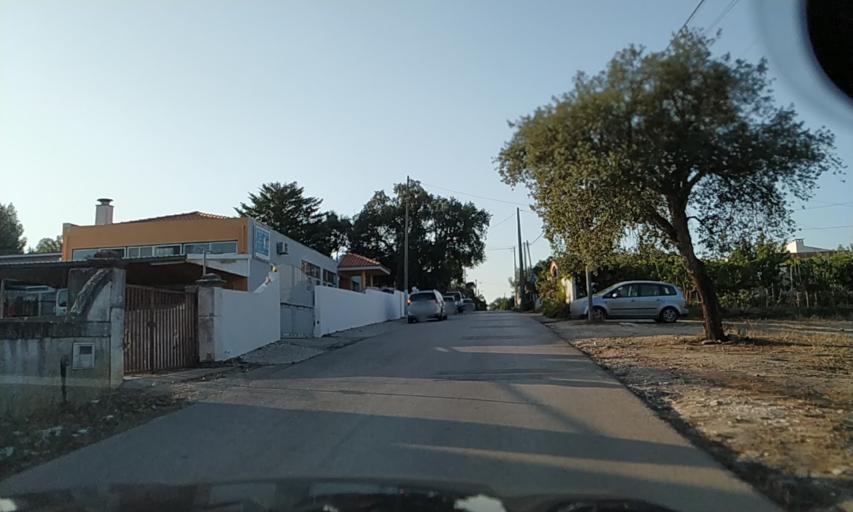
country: PT
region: Setubal
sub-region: Setubal
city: Setubal
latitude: 38.5441
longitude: -8.8393
